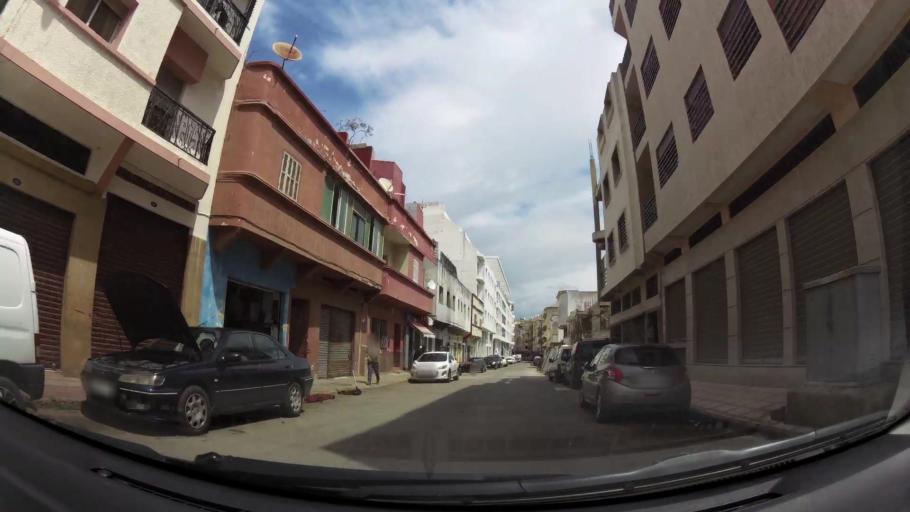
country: MA
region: Grand Casablanca
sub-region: Casablanca
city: Casablanca
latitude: 33.5677
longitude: -7.6540
